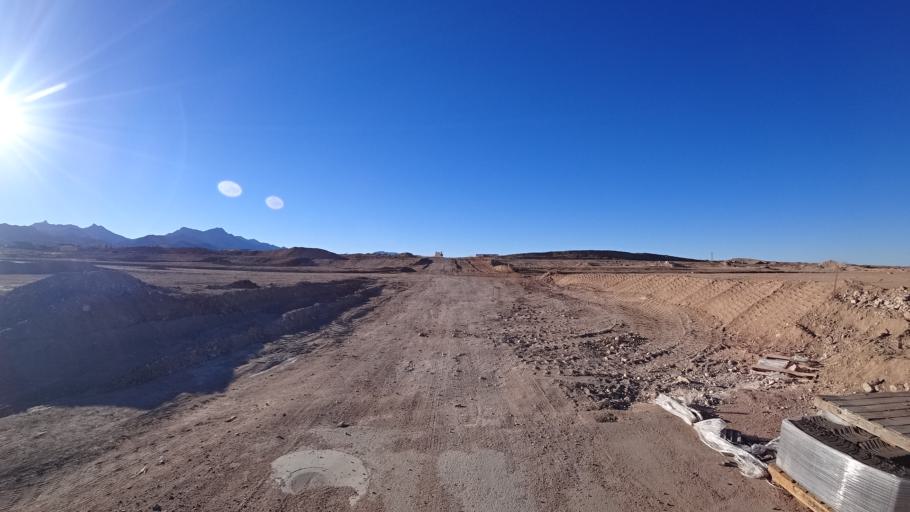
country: US
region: Arizona
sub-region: Mohave County
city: Kingman
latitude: 35.1905
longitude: -113.9982
